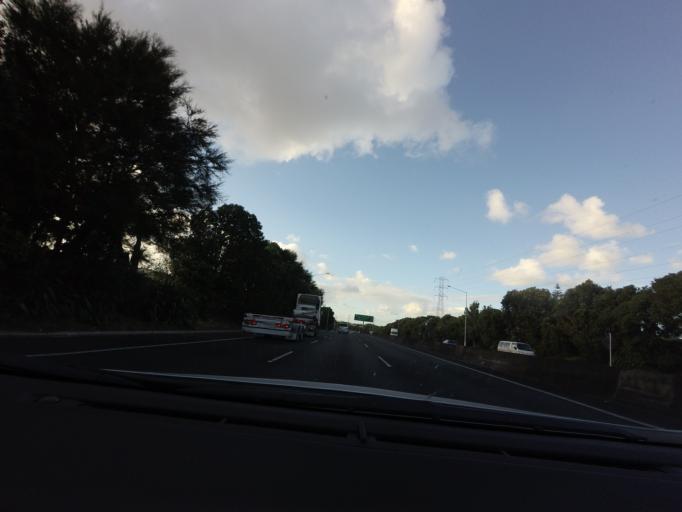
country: NZ
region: Auckland
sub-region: Auckland
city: Manukau City
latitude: -36.9768
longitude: 174.8806
